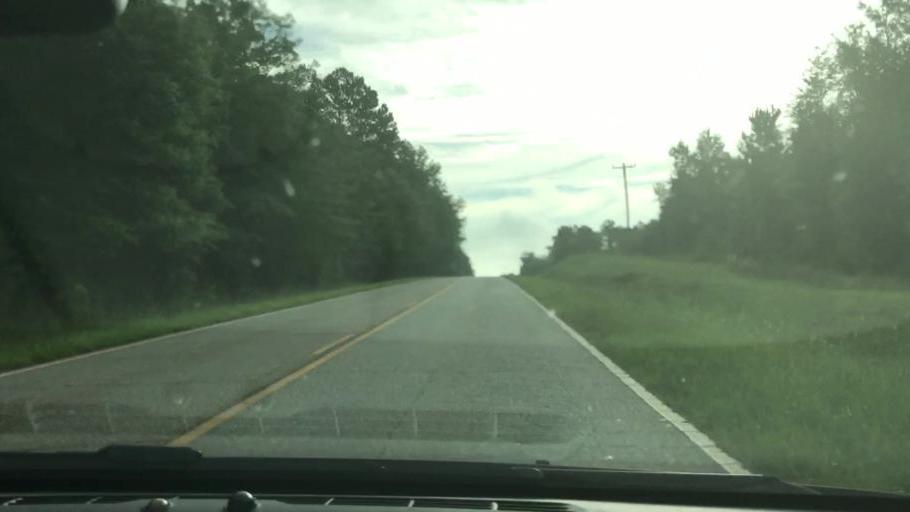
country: US
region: Georgia
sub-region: Quitman County
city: Georgetown
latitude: 31.8941
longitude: -85.0672
